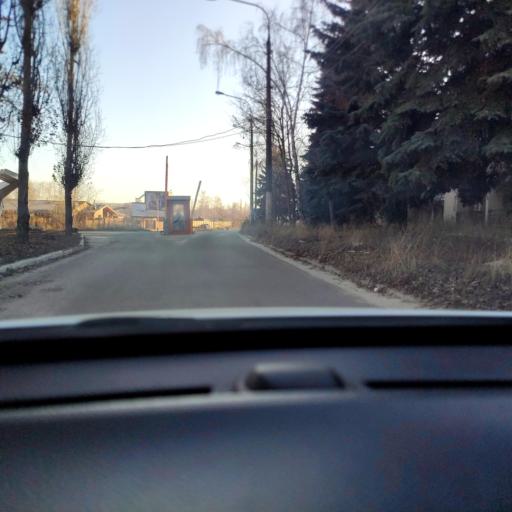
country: RU
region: Voronezj
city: Voronezh
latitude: 51.7260
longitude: 39.2333
